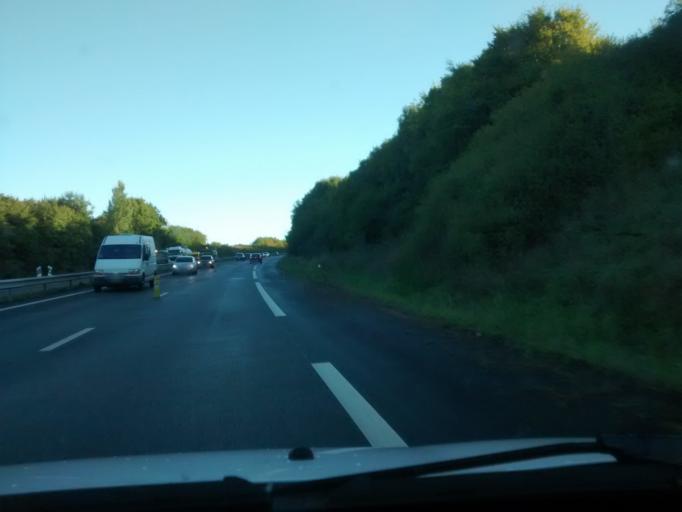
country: FR
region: Brittany
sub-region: Departement d'Ille-et-Vilaine
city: Pleugueneuc
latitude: 48.3974
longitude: -1.9112
